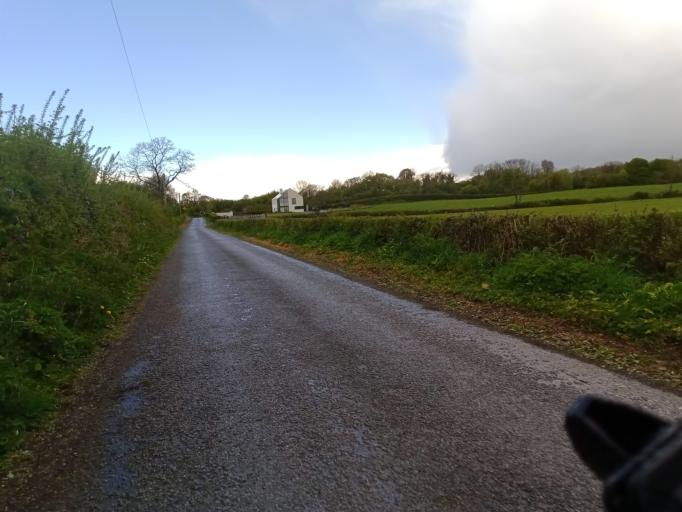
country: IE
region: Leinster
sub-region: Kilkenny
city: Kilkenny
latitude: 52.6922
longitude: -7.2711
